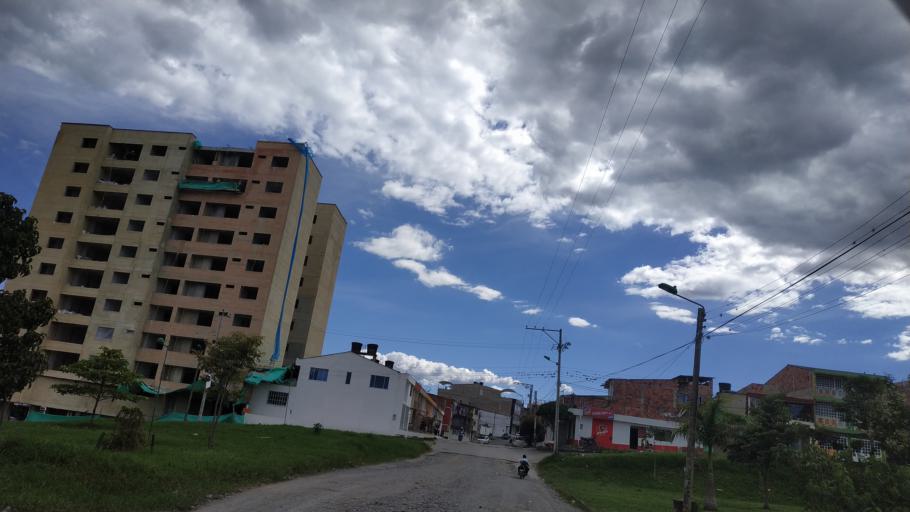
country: CO
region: Santander
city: Barbosa
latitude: 5.9345
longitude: -73.6132
